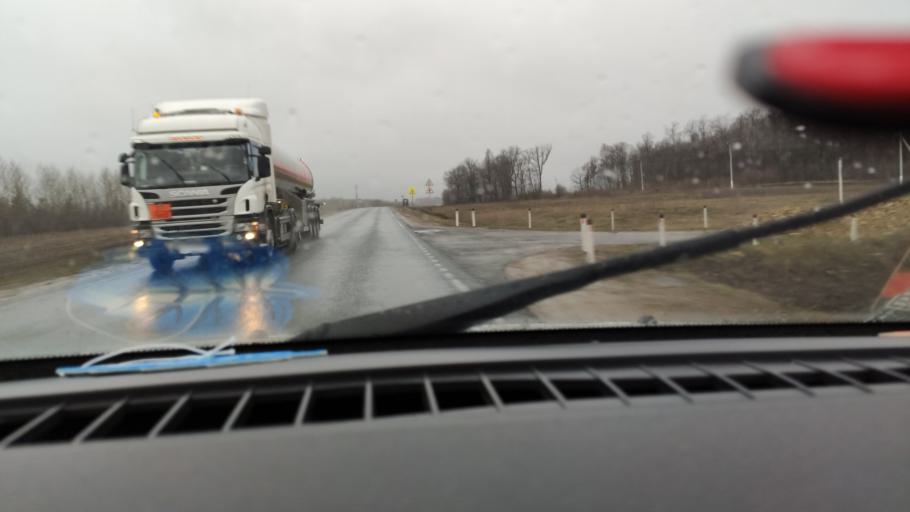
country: RU
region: Tatarstan
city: Cheremshan
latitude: 54.7405
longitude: 51.3513
